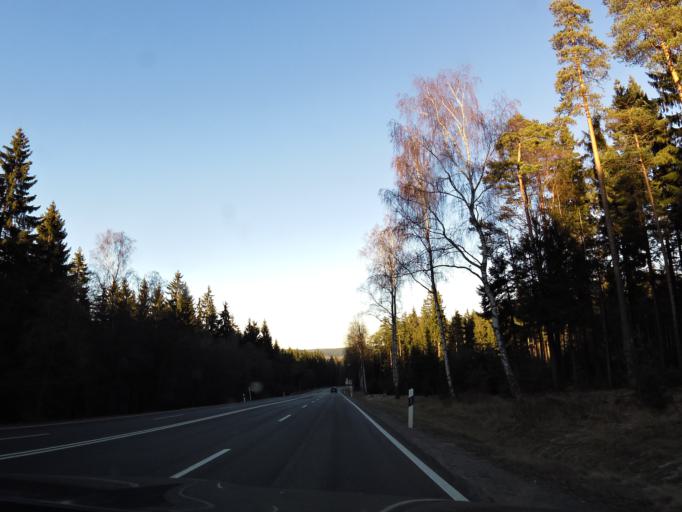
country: DE
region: Bavaria
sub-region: Upper Franconia
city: Trostau
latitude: 50.0095
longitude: 11.9257
